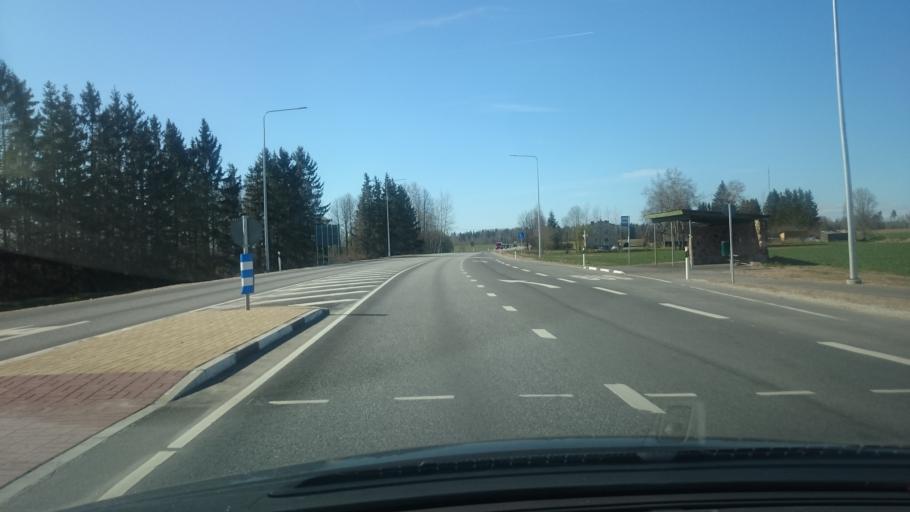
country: EE
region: Tartu
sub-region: Tartu linn
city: Tartu
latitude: 58.3613
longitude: 26.8917
